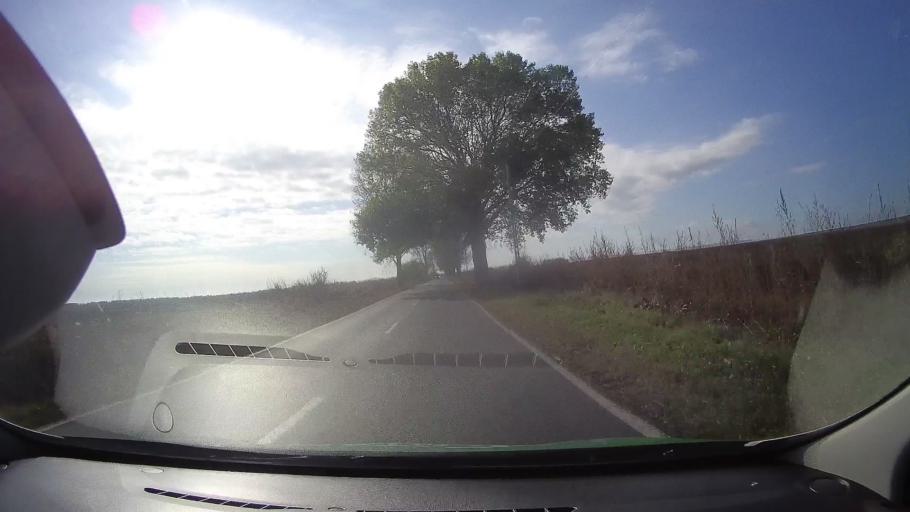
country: RO
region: Tulcea
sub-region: Comuna Valea Nucarilor
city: Agighiol
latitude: 44.9907
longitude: 28.8854
